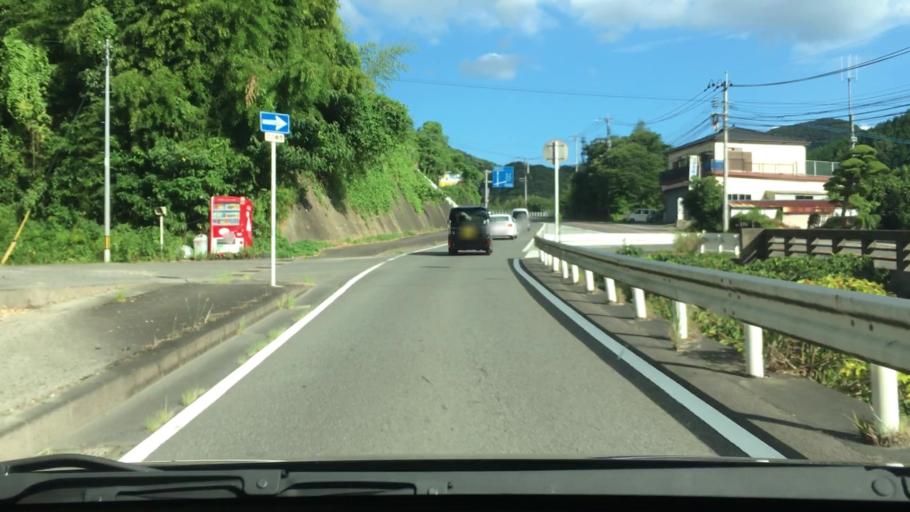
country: JP
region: Nagasaki
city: Togitsu
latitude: 32.8189
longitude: 129.8021
